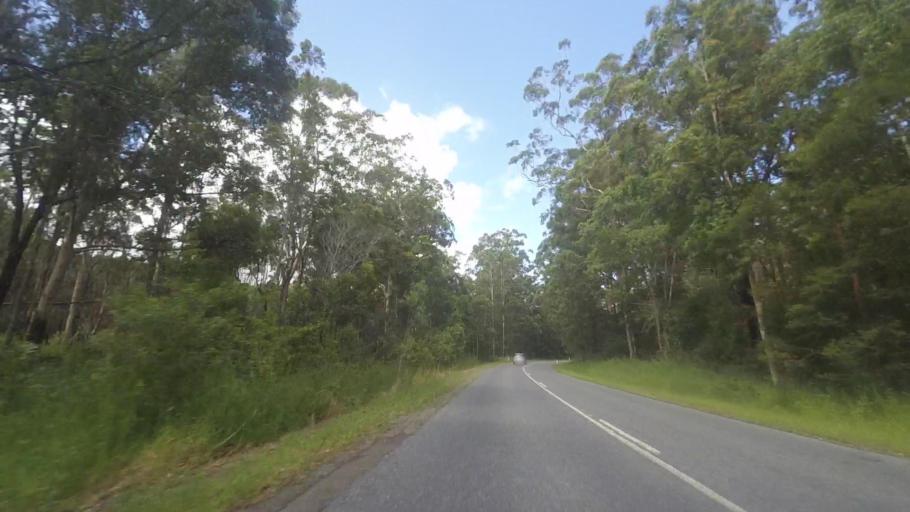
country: AU
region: New South Wales
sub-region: Great Lakes
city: Bulahdelah
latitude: -32.4012
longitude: 152.2848
